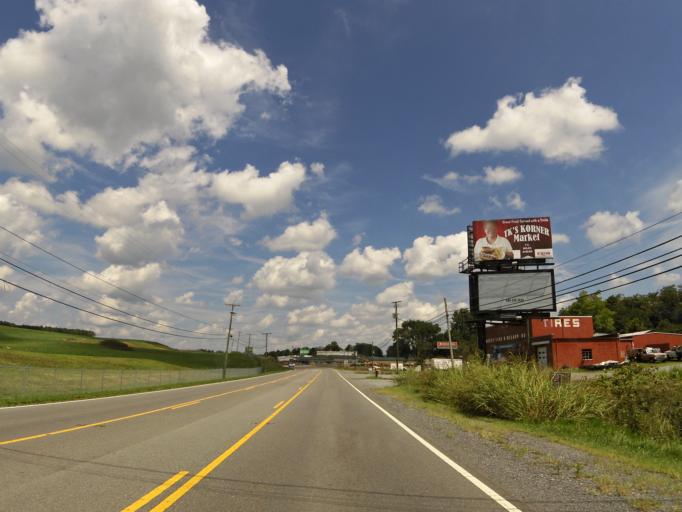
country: US
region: Virginia
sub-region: Washington County
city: Abingdon
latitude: 36.6866
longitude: -82.0300
